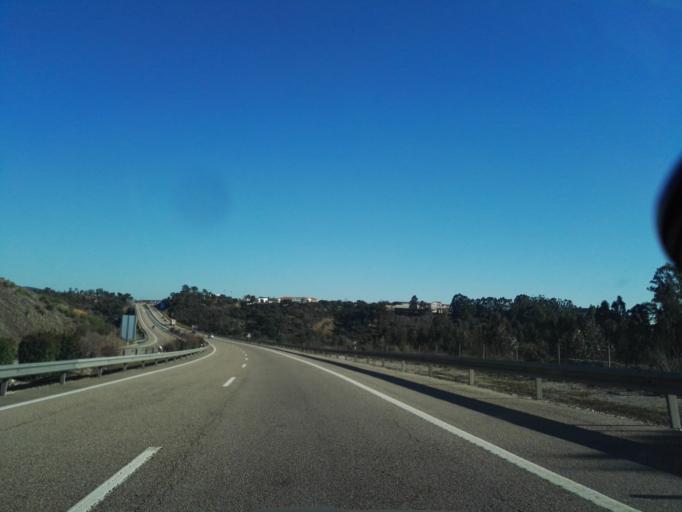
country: PT
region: Santarem
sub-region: Constancia
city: Constancia
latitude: 39.4816
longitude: -8.3472
